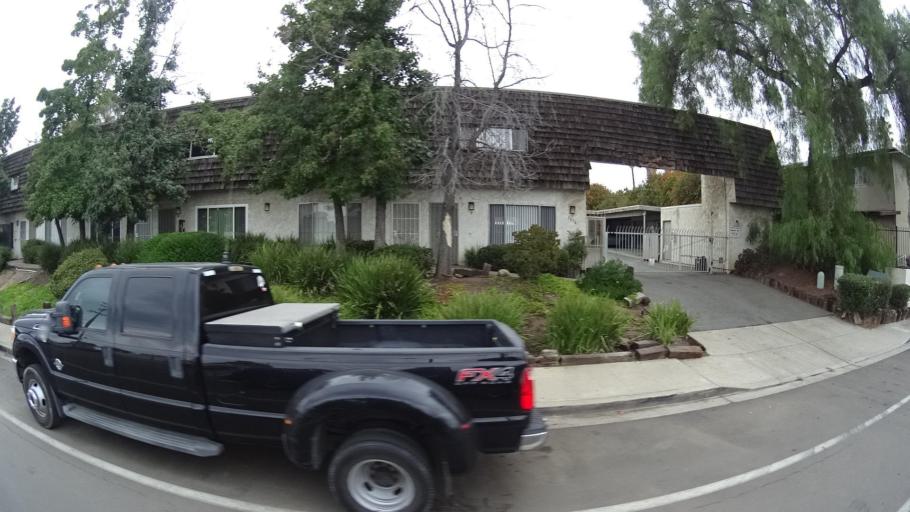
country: US
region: California
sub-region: San Diego County
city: Spring Valley
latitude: 32.7446
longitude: -117.0025
